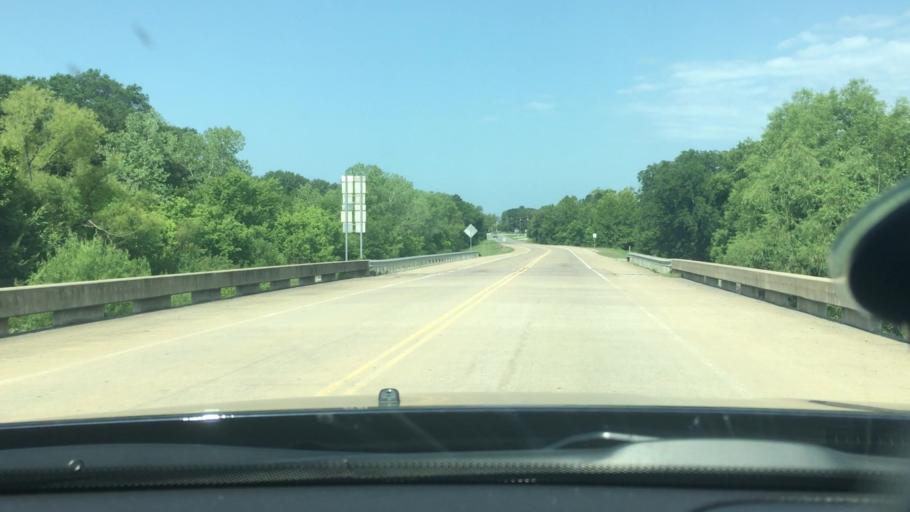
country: US
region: Oklahoma
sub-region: Atoka County
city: Atoka
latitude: 34.3935
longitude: -96.1278
